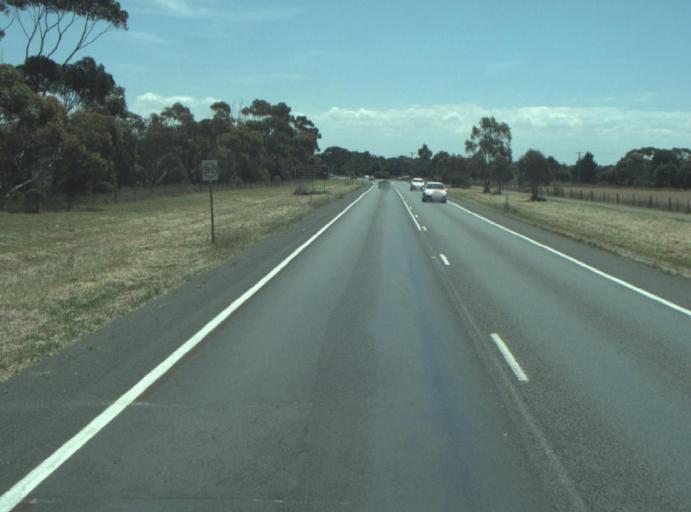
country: AU
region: Victoria
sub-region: Greater Geelong
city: Bell Post Hill
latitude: -38.0992
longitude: 144.3088
